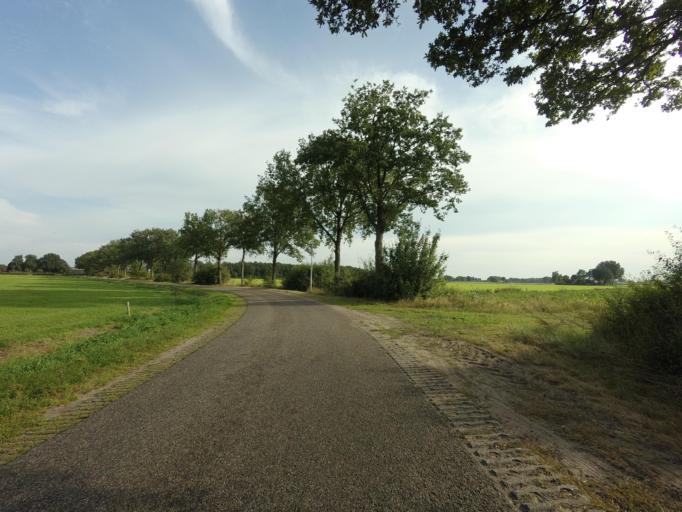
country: DE
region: Lower Saxony
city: Wielen
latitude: 52.5754
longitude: 6.6798
